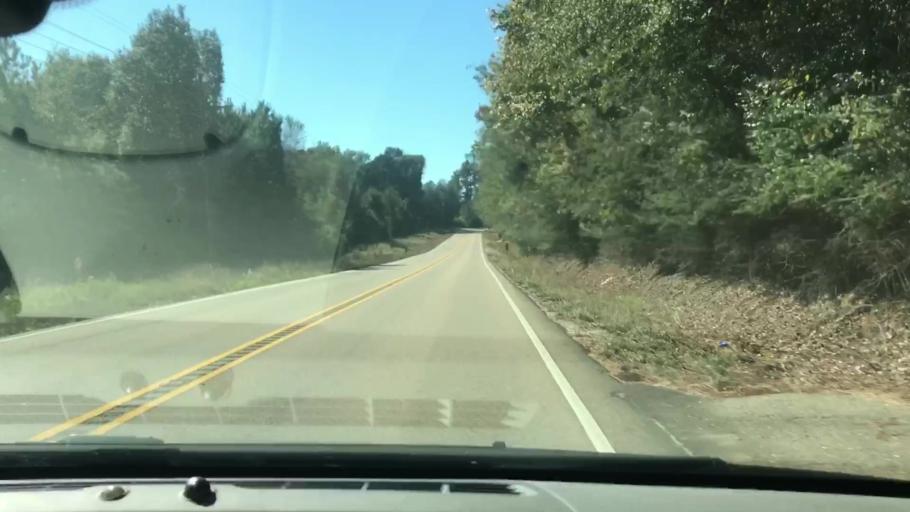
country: US
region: Louisiana
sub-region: Saint Tammany Parish
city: Abita Springs
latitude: 30.5100
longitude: -89.9504
